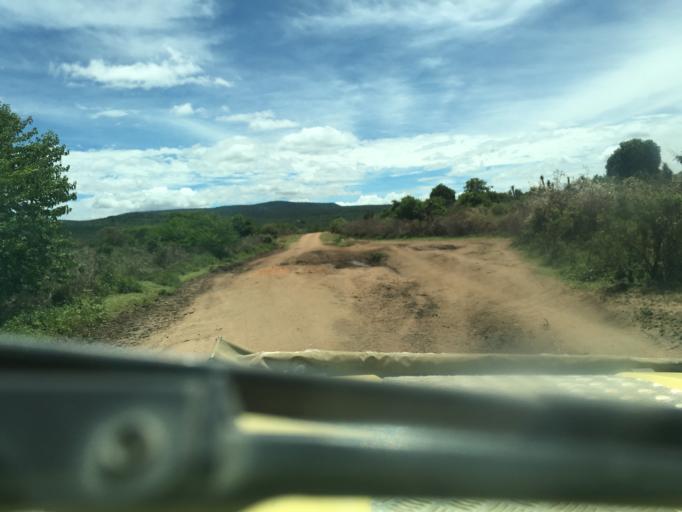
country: TZ
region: Mara
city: Mugumu
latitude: -1.8886
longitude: 35.3713
